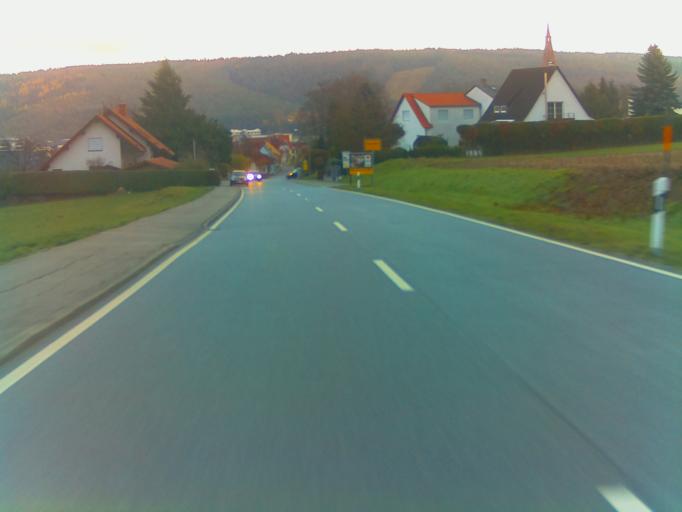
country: DE
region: Hesse
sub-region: Regierungsbezirk Darmstadt
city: Beerfelden
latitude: 49.5707
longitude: 8.9683
